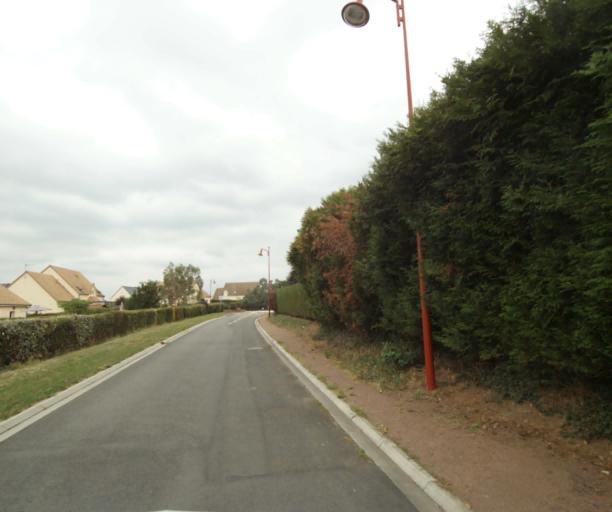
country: FR
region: Pays de la Loire
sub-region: Departement de la Sarthe
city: Solesmes
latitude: 47.8513
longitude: -0.2922
